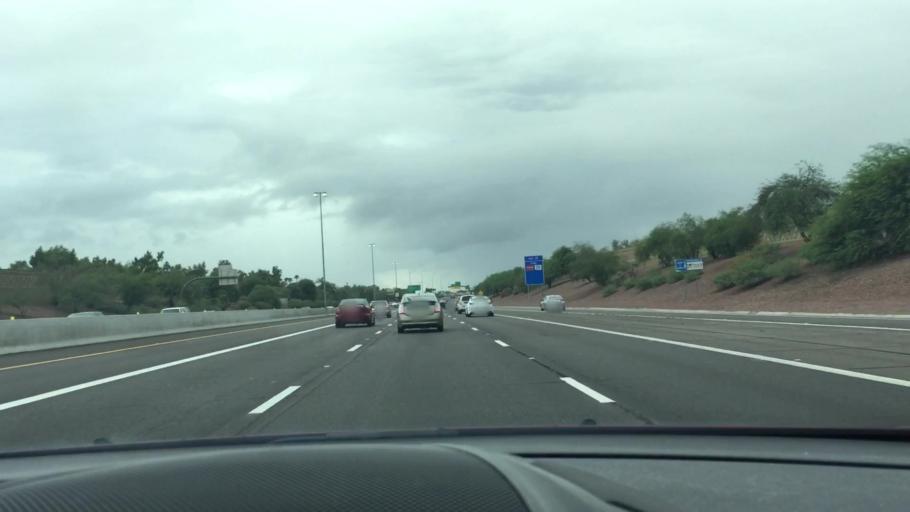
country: US
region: Arizona
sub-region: Maricopa County
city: Peoria
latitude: 33.6671
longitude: -112.2067
